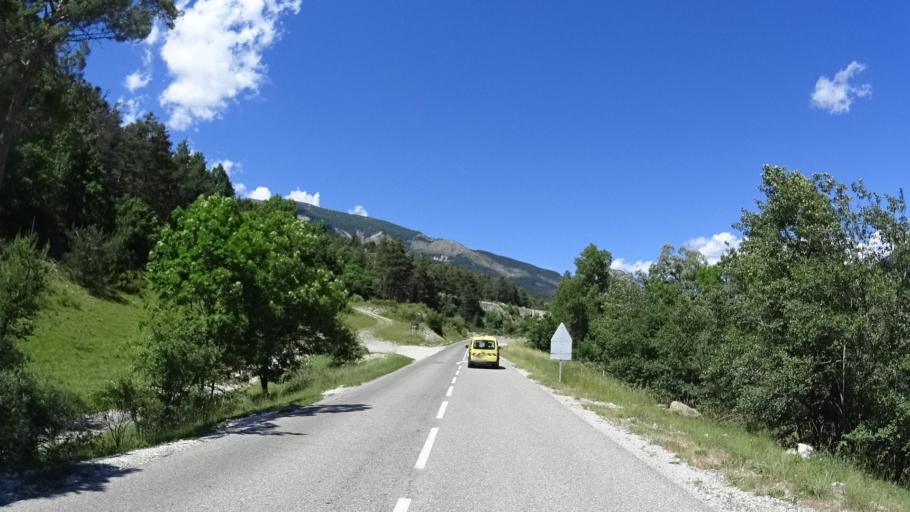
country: FR
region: Provence-Alpes-Cote d'Azur
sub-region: Departement des Alpes-de-Haute-Provence
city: Annot
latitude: 44.1283
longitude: 6.5806
